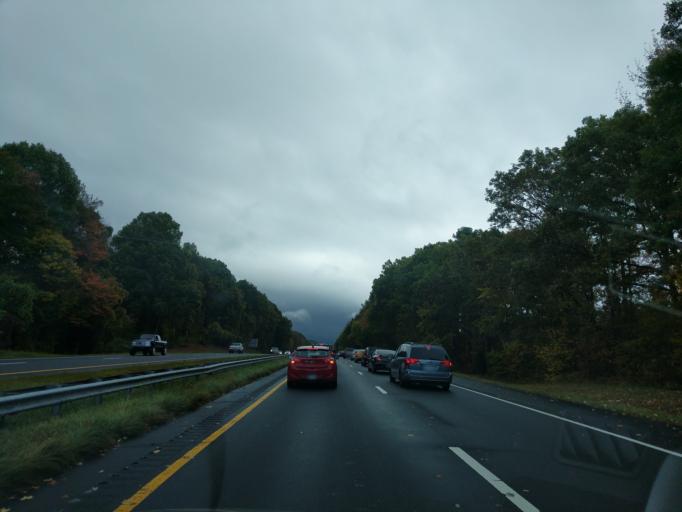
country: US
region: North Carolina
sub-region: Orange County
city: Hillsborough
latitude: 36.0569
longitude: -79.0760
